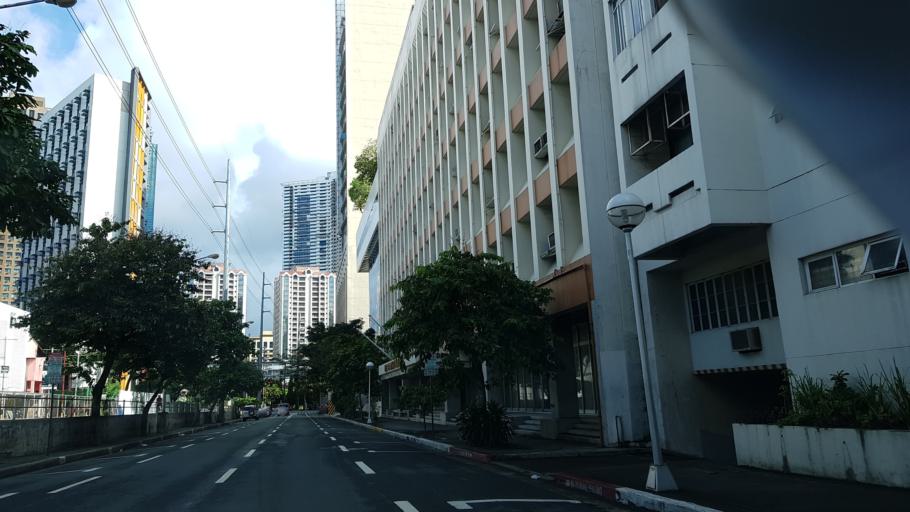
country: PH
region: Metro Manila
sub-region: Makati City
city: Makati City
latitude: 14.5570
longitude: 121.0143
